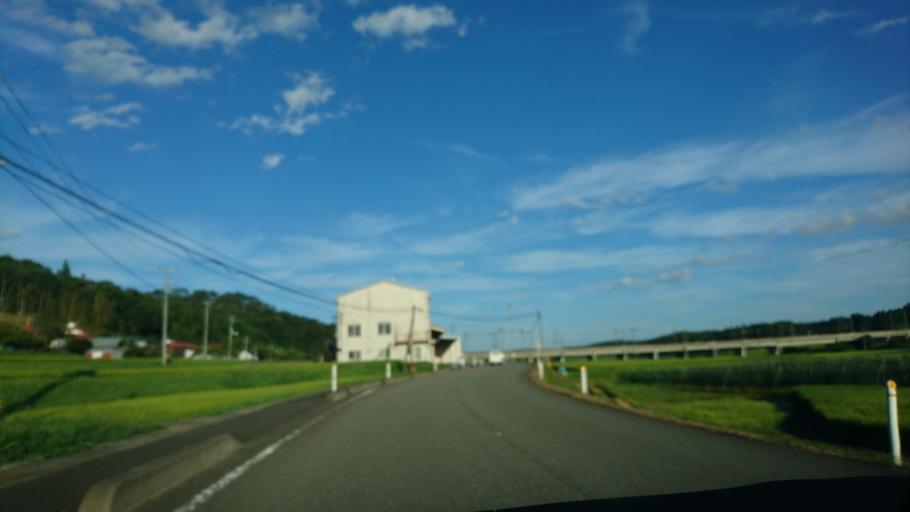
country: JP
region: Iwate
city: Ichinoseki
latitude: 38.8498
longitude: 141.1073
